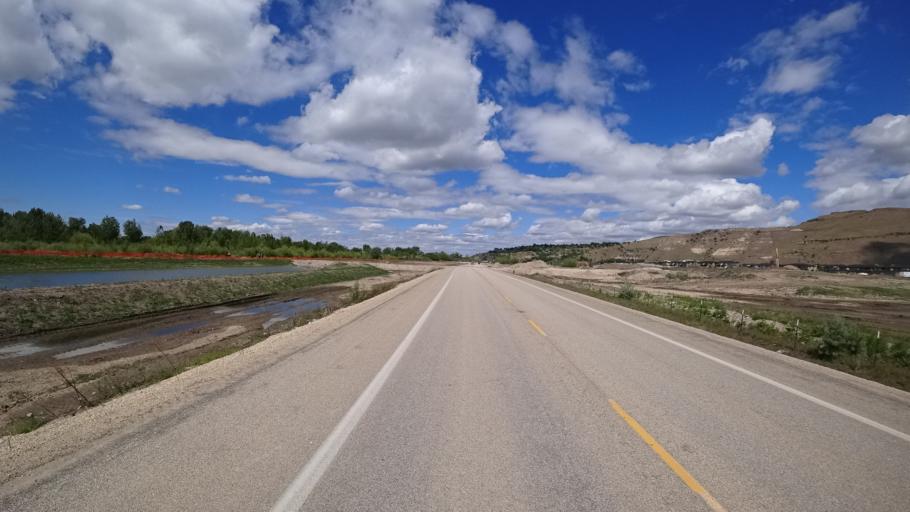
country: US
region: Idaho
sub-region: Ada County
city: Boise
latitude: 43.5711
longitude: -116.1344
